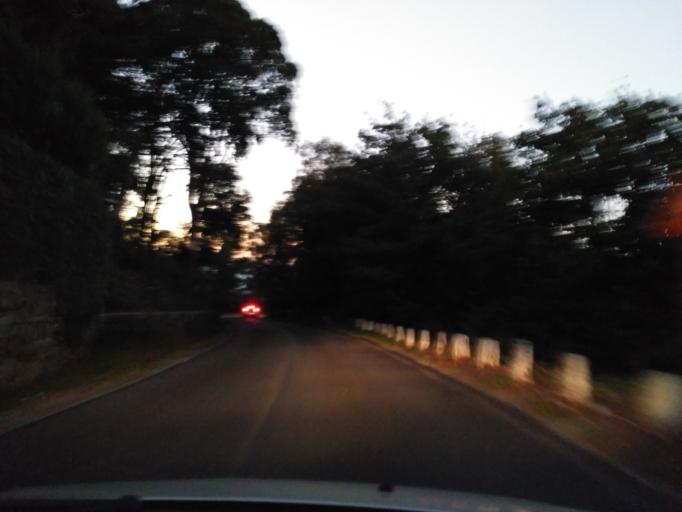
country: PT
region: Braga
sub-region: Braga
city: Adaufe
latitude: 41.5547
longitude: -8.3740
